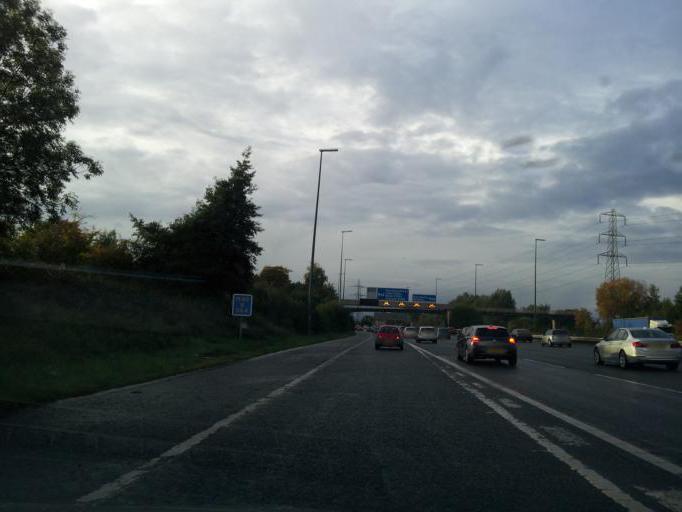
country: GB
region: England
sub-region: Manchester
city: Crumpsall
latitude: 53.5426
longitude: -2.2442
